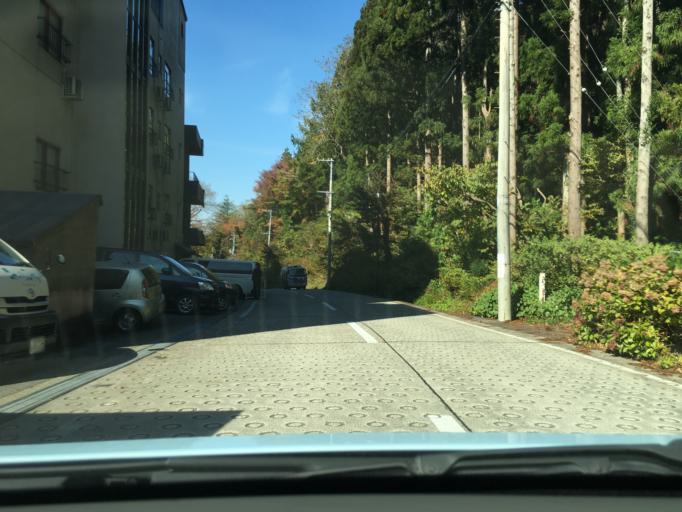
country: JP
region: Fukushima
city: Inawashiro
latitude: 37.4792
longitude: 139.9631
